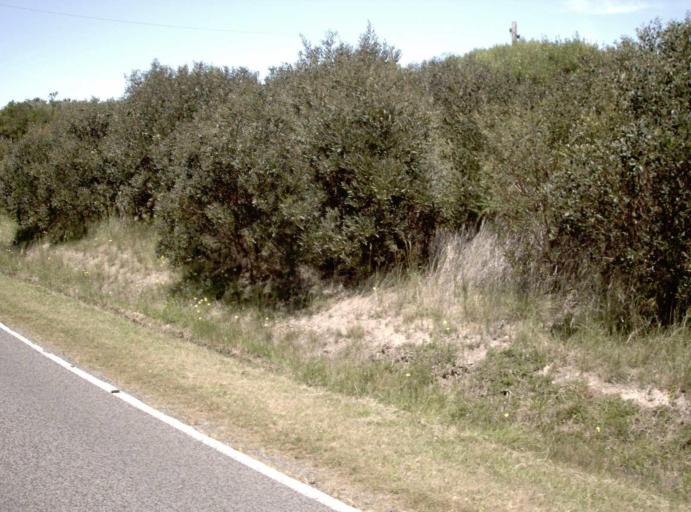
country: AU
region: Victoria
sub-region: Bass Coast
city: North Wonthaggi
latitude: -38.7694
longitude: 146.1578
